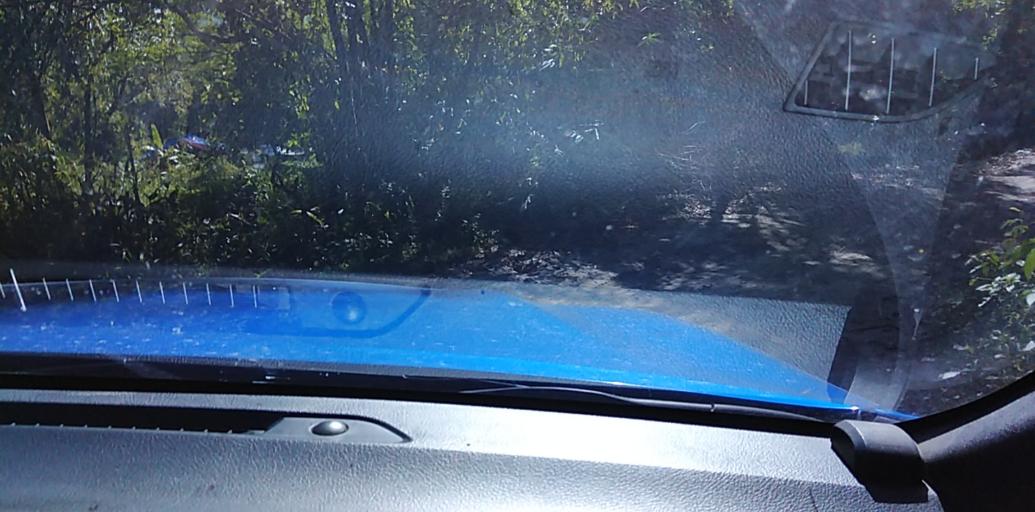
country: PH
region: Central Luzon
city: Santol
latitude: 15.1678
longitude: 120.4885
